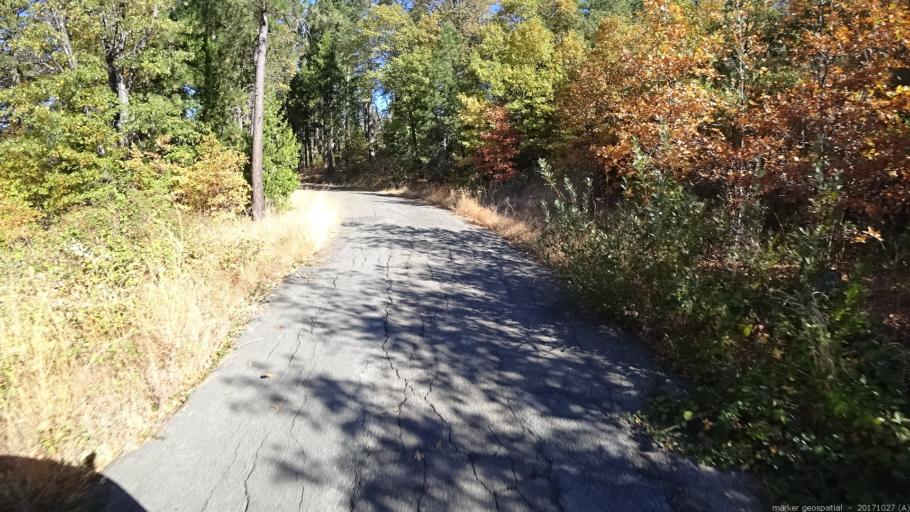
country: US
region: California
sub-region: Shasta County
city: Burney
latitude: 40.8016
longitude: -121.8965
